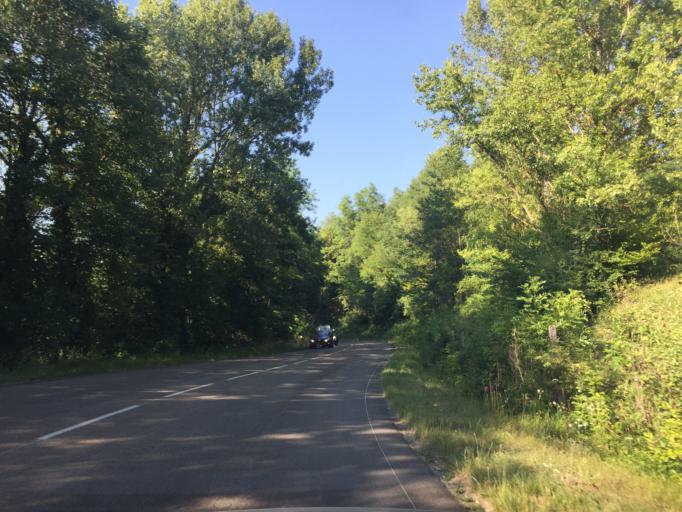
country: FR
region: Rhone-Alpes
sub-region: Departement de la Drome
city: Saint-Jean-en-Royans
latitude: 45.0401
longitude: 5.3023
